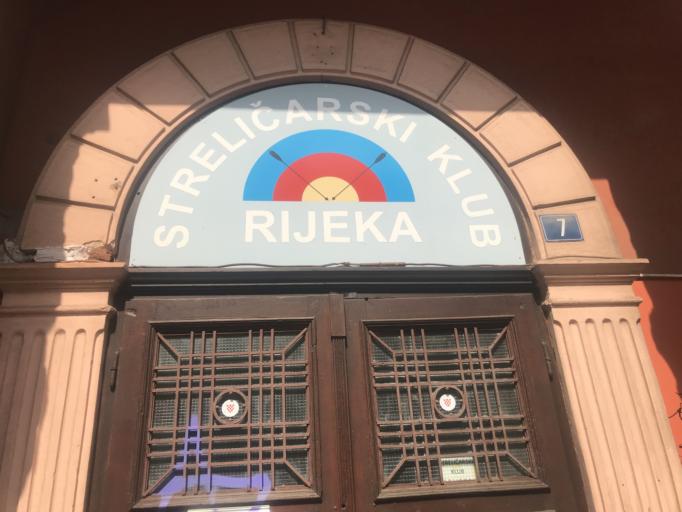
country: HR
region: Primorsko-Goranska
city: Drenova
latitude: 45.3285
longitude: 14.4500
